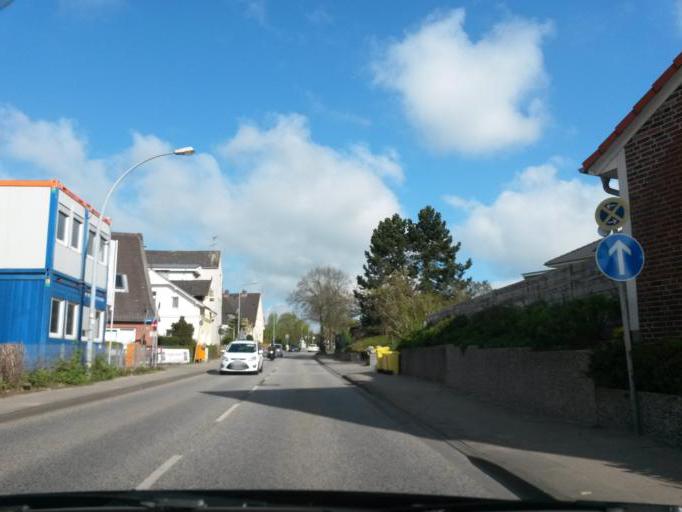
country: DE
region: Schleswig-Holstein
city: Wedel
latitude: 53.5869
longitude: 9.6917
